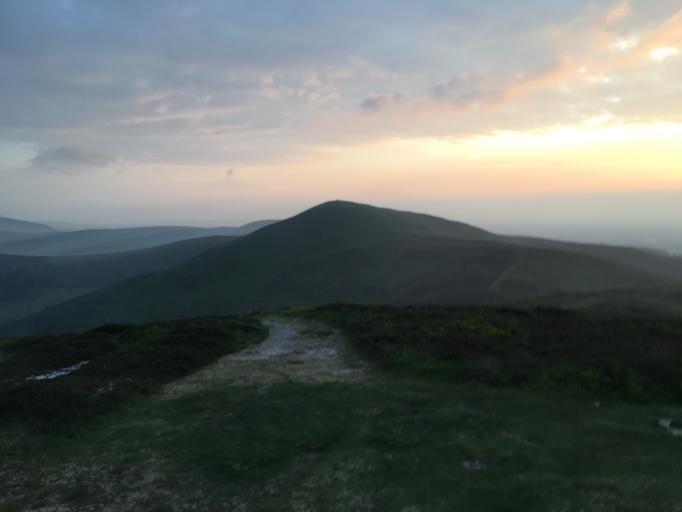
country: GB
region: Scotland
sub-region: Edinburgh
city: Colinton
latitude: 55.8826
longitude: -3.2236
